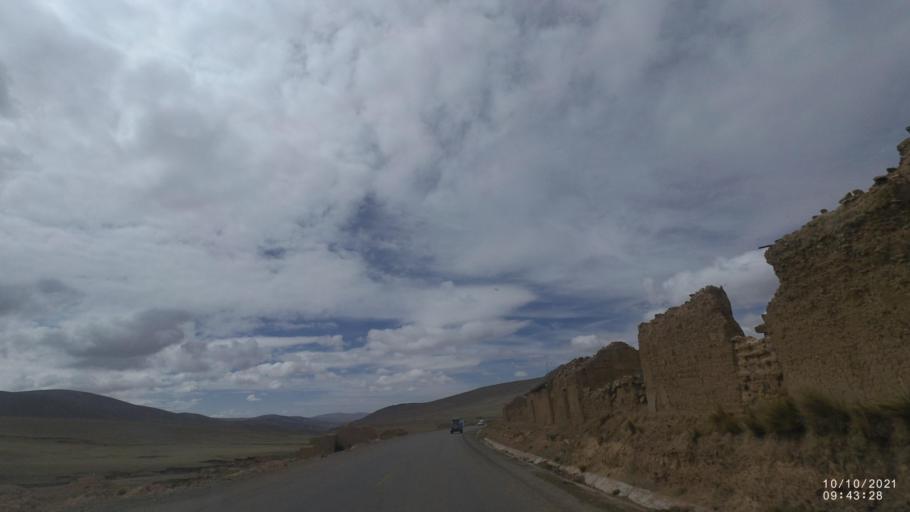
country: BO
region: La Paz
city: Quime
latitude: -17.1503
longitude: -67.3451
